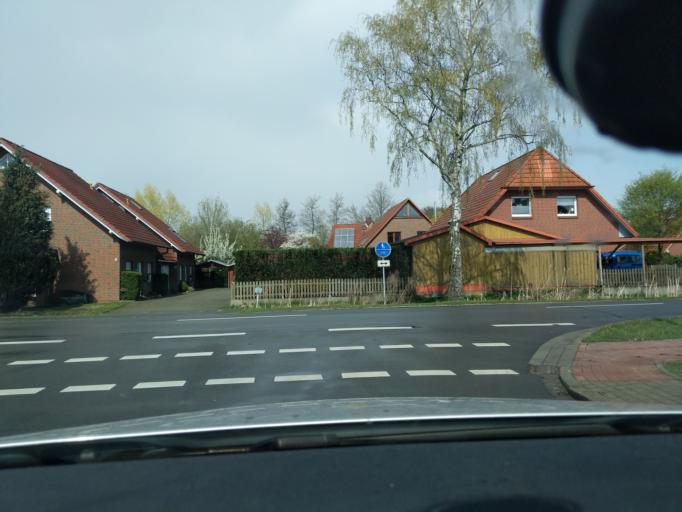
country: DE
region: Lower Saxony
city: Ahlerstedt
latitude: 53.4057
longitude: 9.4493
